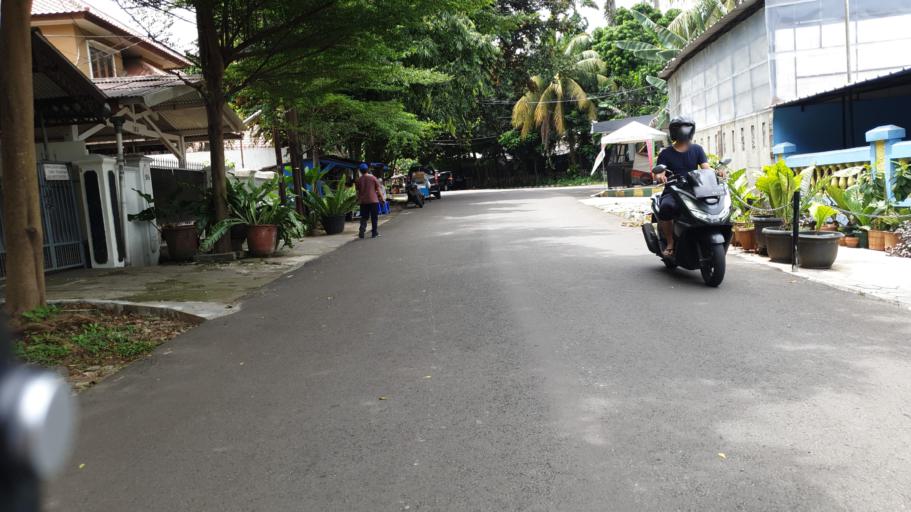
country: ID
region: West Java
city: Pamulang
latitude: -6.2968
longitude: 106.7799
